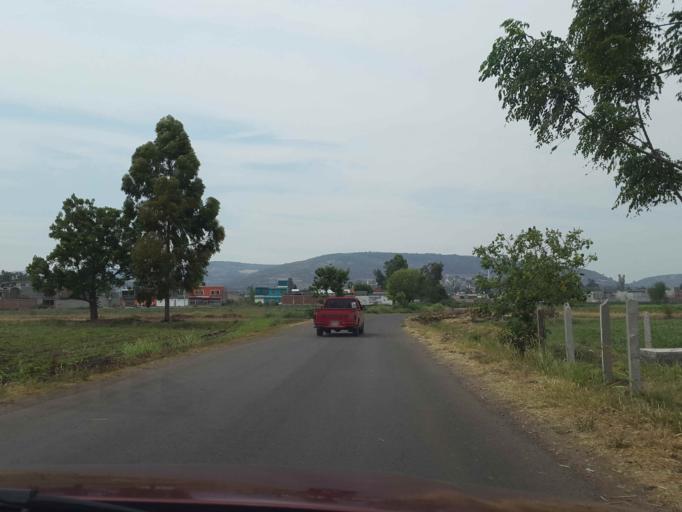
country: MX
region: Michoacan
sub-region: Tarimbaro
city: El Colegio
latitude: 19.7875
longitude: -101.1777
